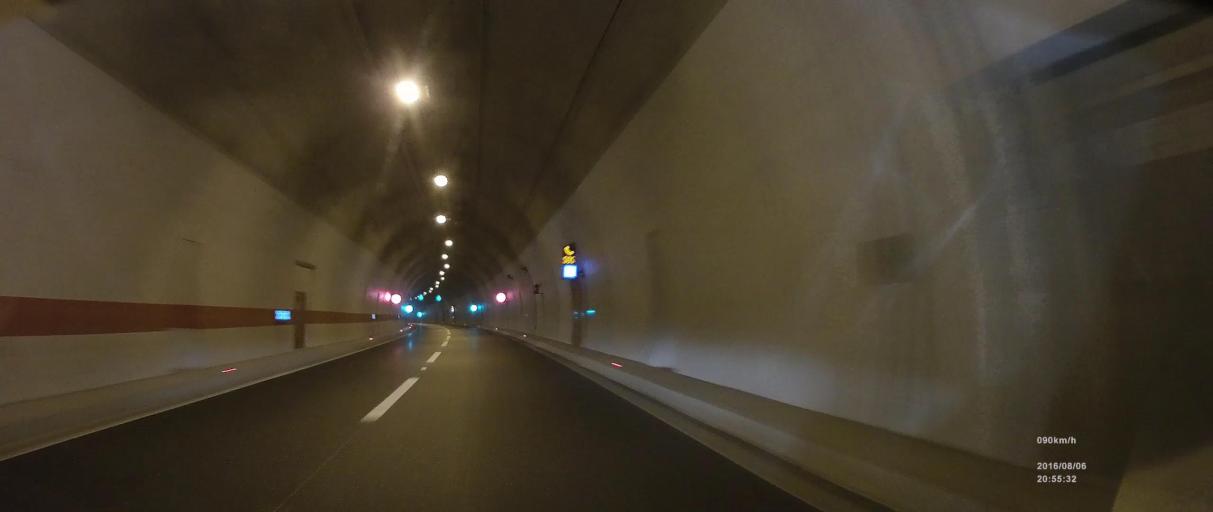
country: BA
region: Federation of Bosnia and Herzegovina
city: Vitina
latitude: 43.1623
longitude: 17.4702
